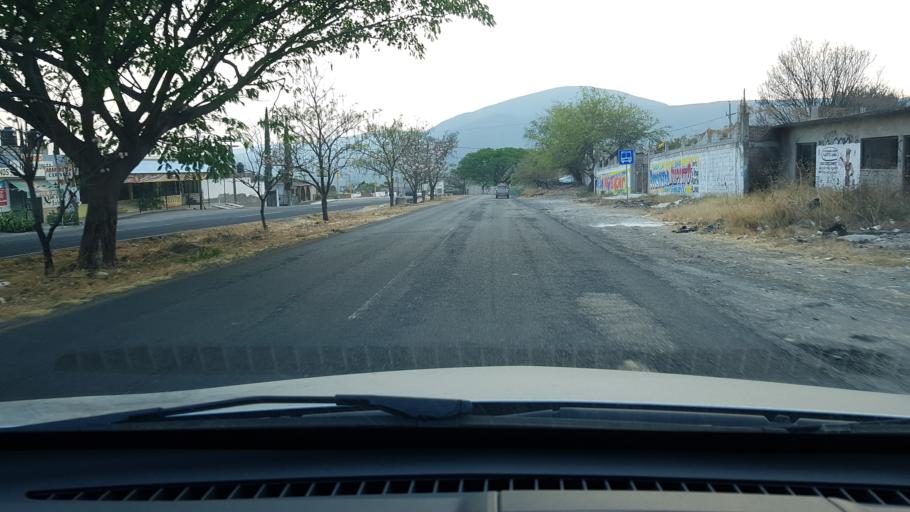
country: MX
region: Morelos
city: Yautepec
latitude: 18.8671
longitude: -99.0861
